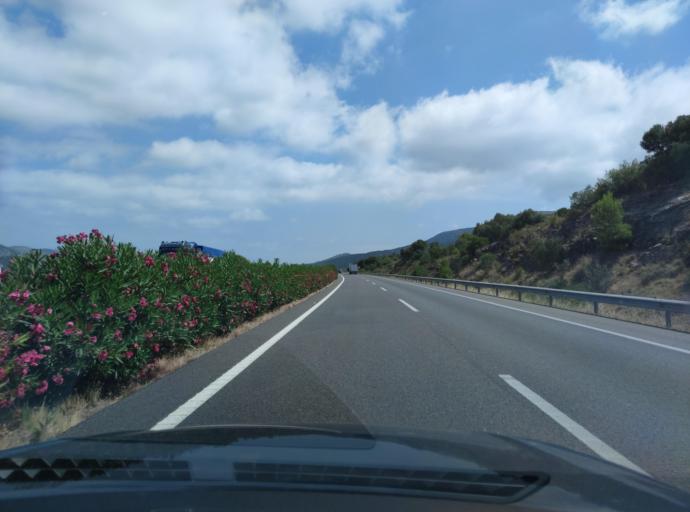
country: ES
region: Valencia
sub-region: Provincia de Castello
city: Santa Magdalena de Pulpis
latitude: 40.3568
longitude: 0.3160
